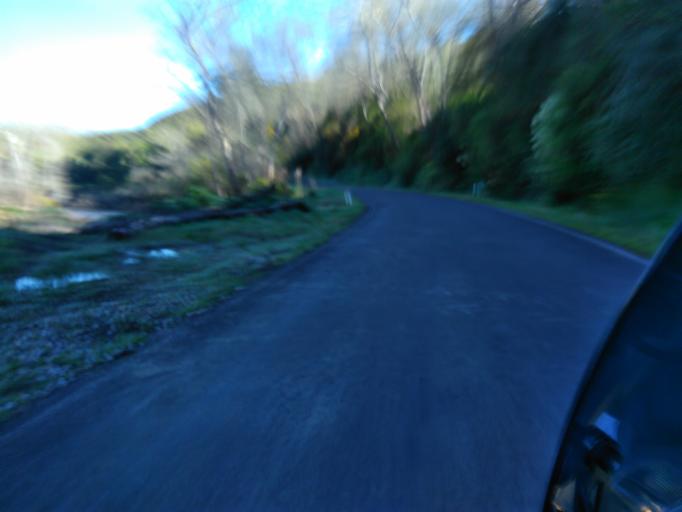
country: NZ
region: Gisborne
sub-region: Gisborne District
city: Gisborne
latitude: -38.4329
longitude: 177.7431
